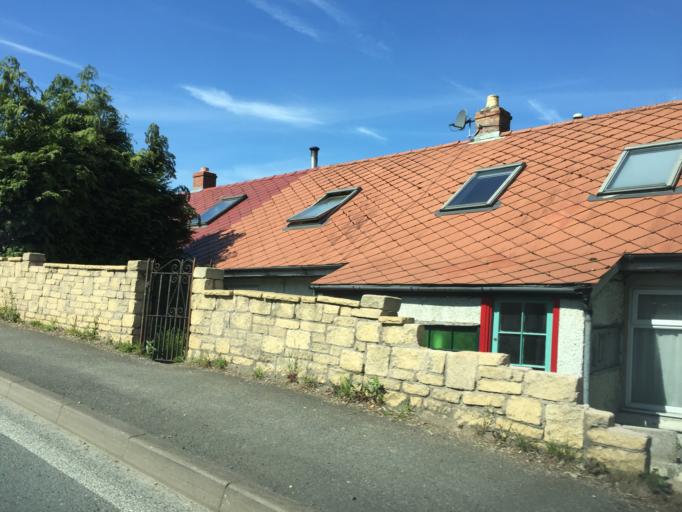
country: GB
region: England
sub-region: Gloucestershire
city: Nailsworth
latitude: 51.6863
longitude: -2.2230
